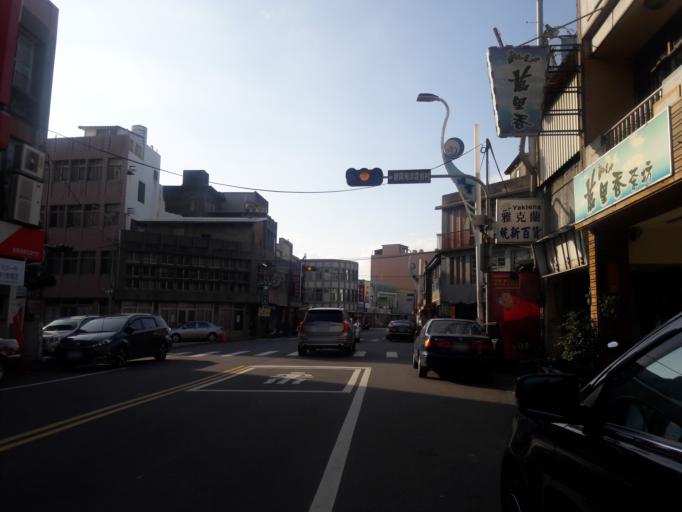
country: TW
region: Taiwan
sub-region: Miaoli
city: Miaoli
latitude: 24.4903
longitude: 120.6806
